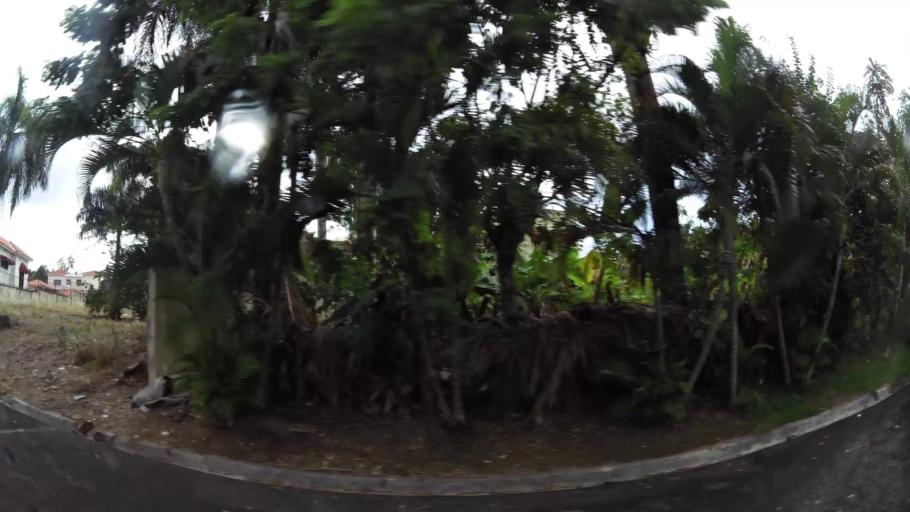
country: DO
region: Nacional
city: Santo Domingo
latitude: 18.5025
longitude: -69.9711
